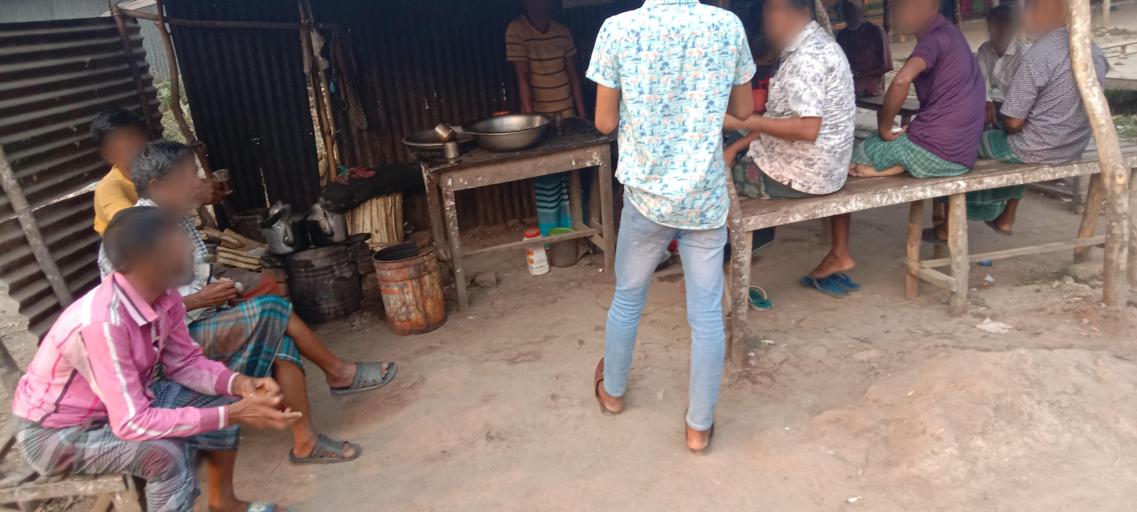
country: BD
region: Dhaka
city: Sakhipur
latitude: 24.3250
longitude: 90.3033
